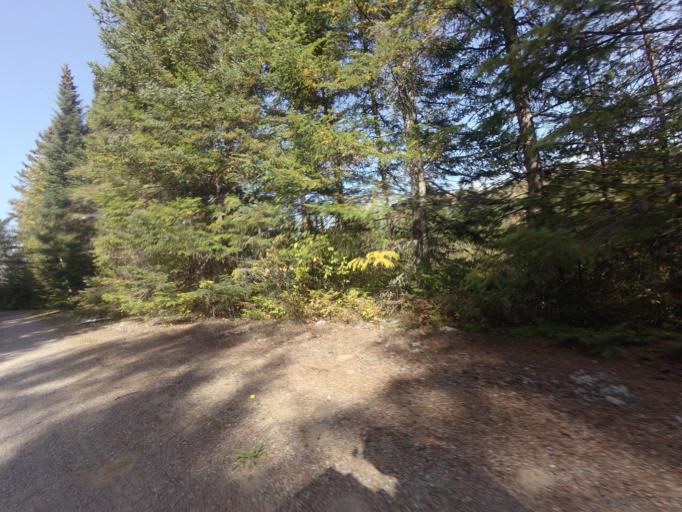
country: CA
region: Quebec
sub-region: Laurentides
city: Sainte-Agathe-des-Monts
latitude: 46.0784
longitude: -74.3193
